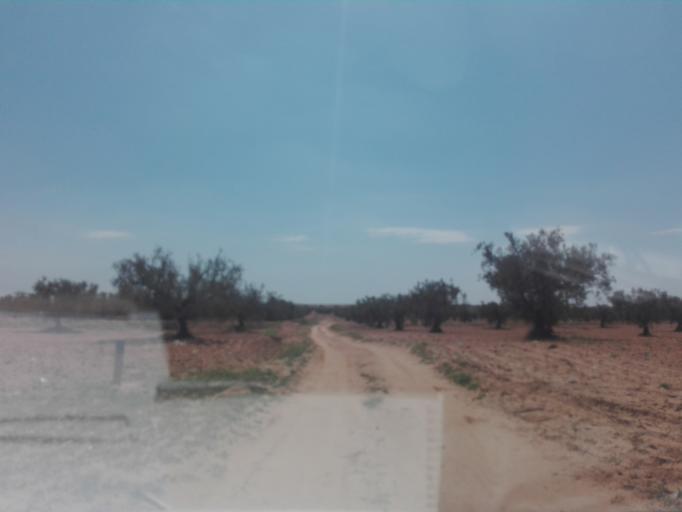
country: TN
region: Safaqis
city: Bi'r `Ali Bin Khalifah
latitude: 34.6109
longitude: 10.3527
